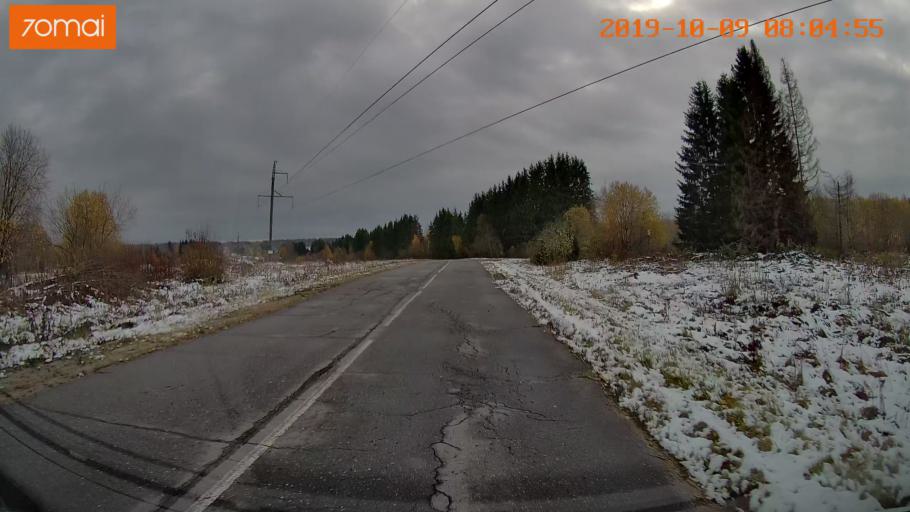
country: RU
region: Jaroslavl
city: Kukoboy
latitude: 58.6909
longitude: 40.0350
